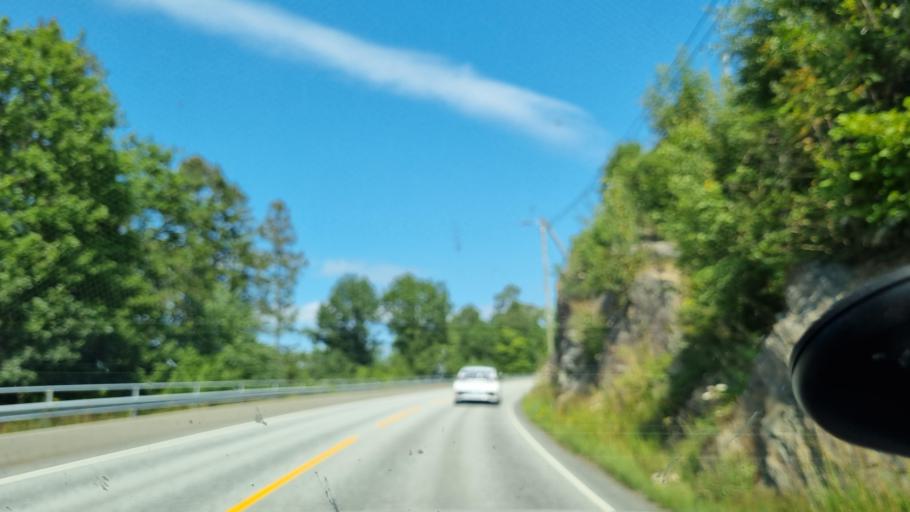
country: NO
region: Aust-Agder
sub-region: Arendal
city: Arendal
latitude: 58.4621
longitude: 8.8195
